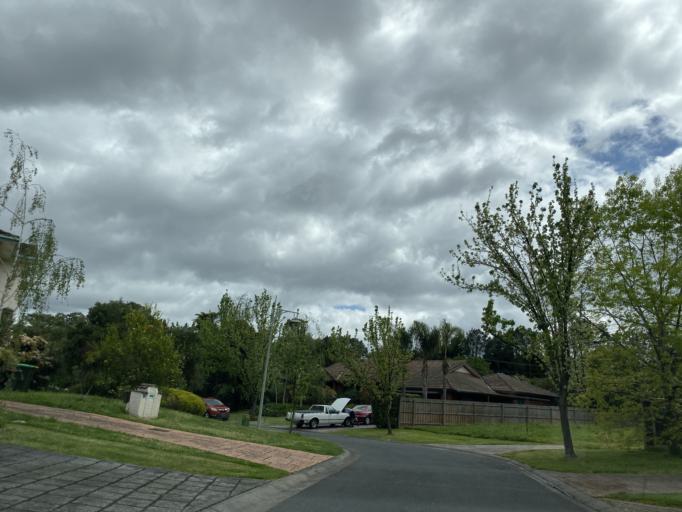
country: AU
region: Victoria
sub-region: Nillumbik
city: Eltham
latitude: -37.7543
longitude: 145.1430
